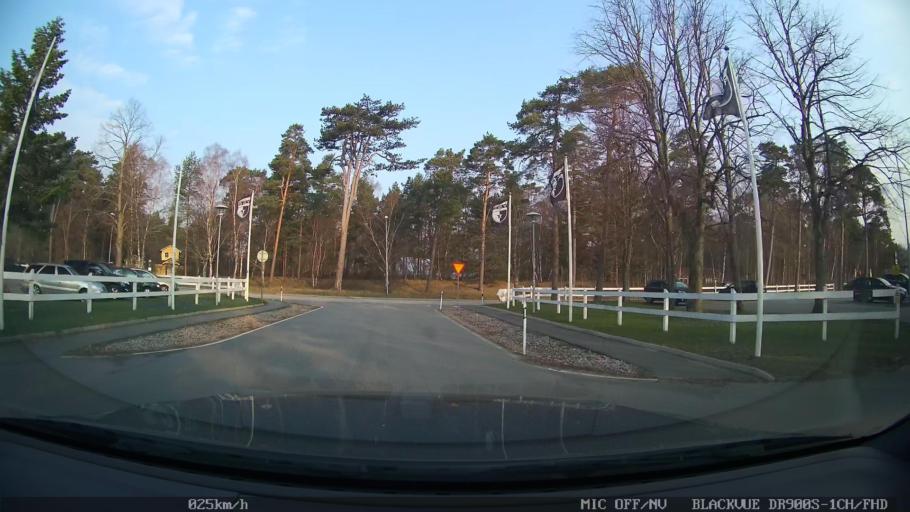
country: SE
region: Skane
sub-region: Ystads Kommun
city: Ystad
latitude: 55.4256
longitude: 13.8482
